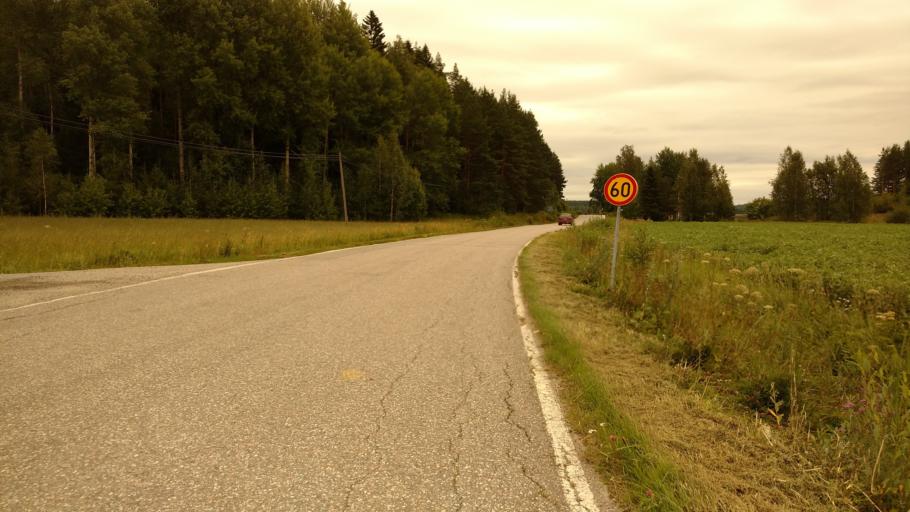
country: FI
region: Varsinais-Suomi
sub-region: Loimaa
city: Marttila
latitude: 60.4158
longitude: 22.8709
